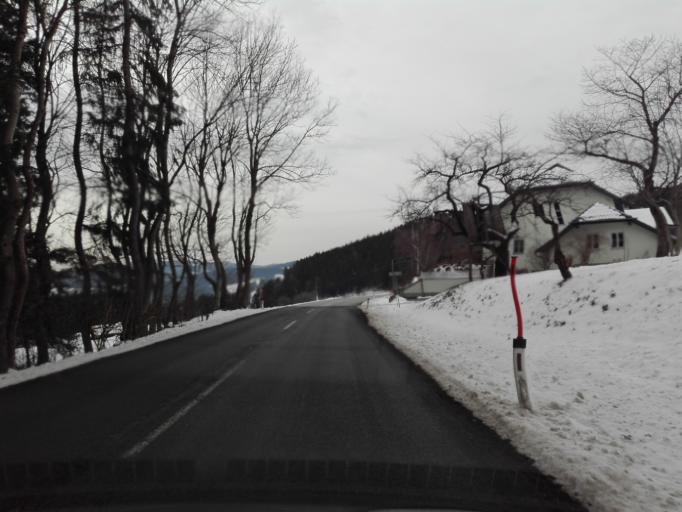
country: DE
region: Bavaria
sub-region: Lower Bavaria
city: Wegscheid
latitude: 48.5544
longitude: 13.8058
